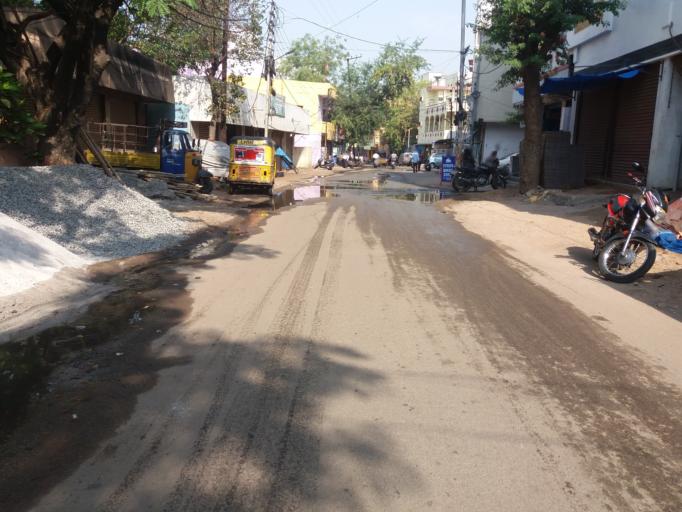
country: IN
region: Telangana
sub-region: Hyderabad
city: Malkajgiri
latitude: 17.4160
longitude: 78.5091
